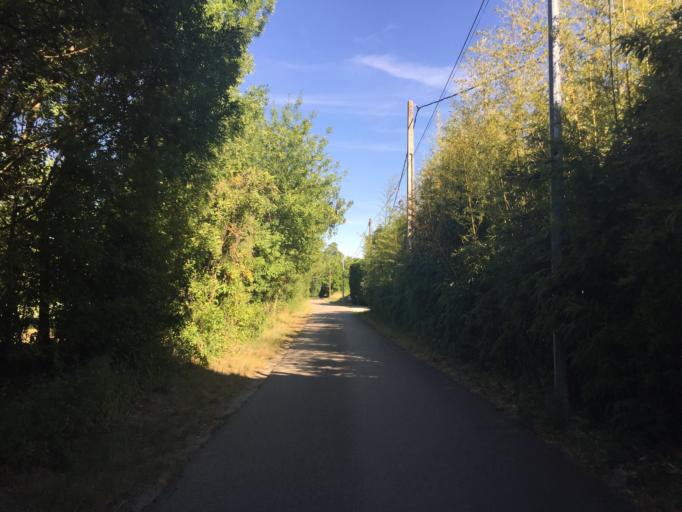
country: FR
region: Provence-Alpes-Cote d'Azur
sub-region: Departement du Vaucluse
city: Caderousse
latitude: 44.1247
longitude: 4.7209
